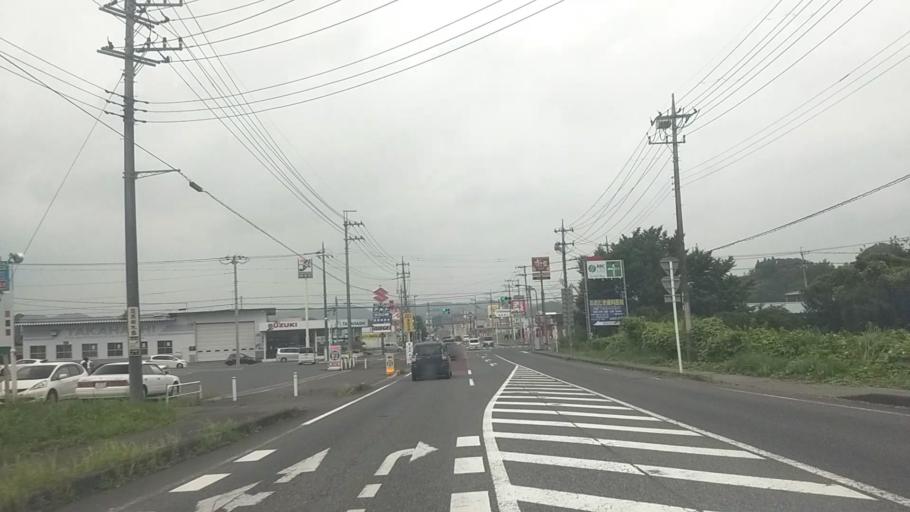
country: JP
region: Chiba
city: Ohara
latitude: 35.2851
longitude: 140.2524
